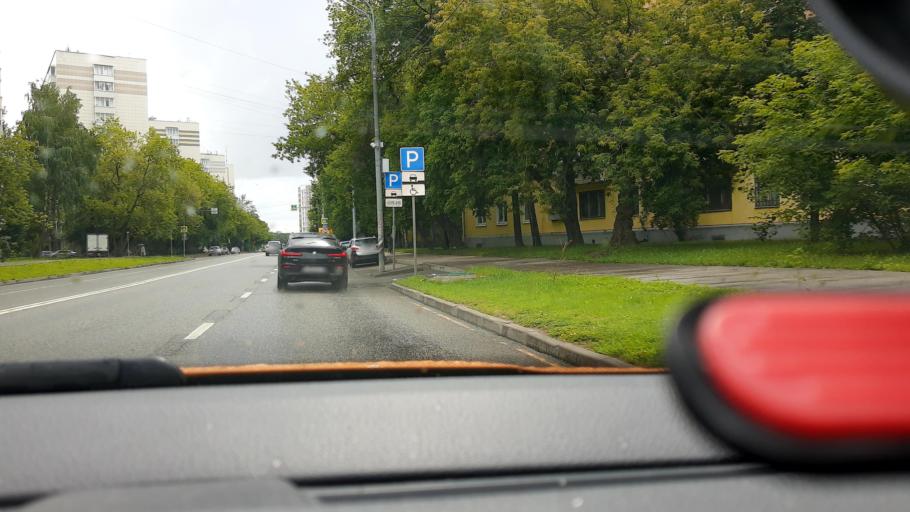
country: RU
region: Moscow
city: Leonovo
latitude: 55.8505
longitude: 37.6450
